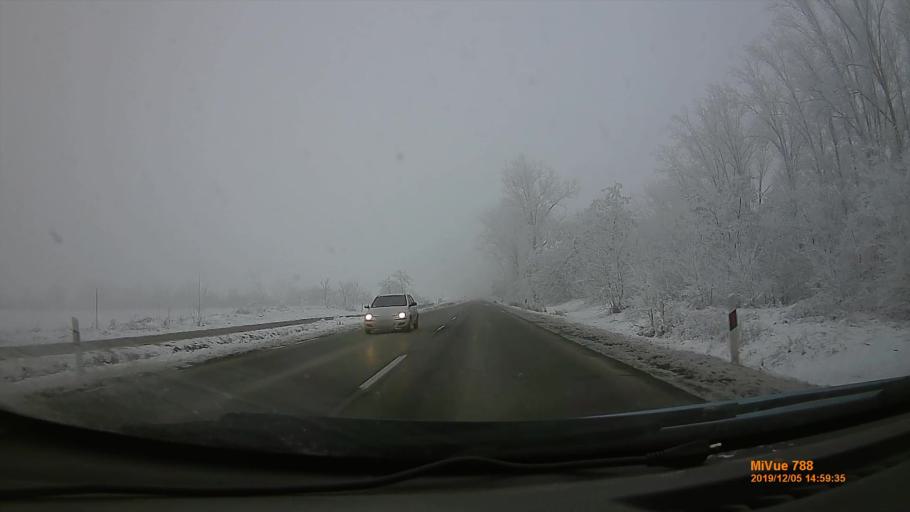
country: HU
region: Szabolcs-Szatmar-Bereg
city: Tiszanagyfalu
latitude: 48.0582
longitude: 21.5548
